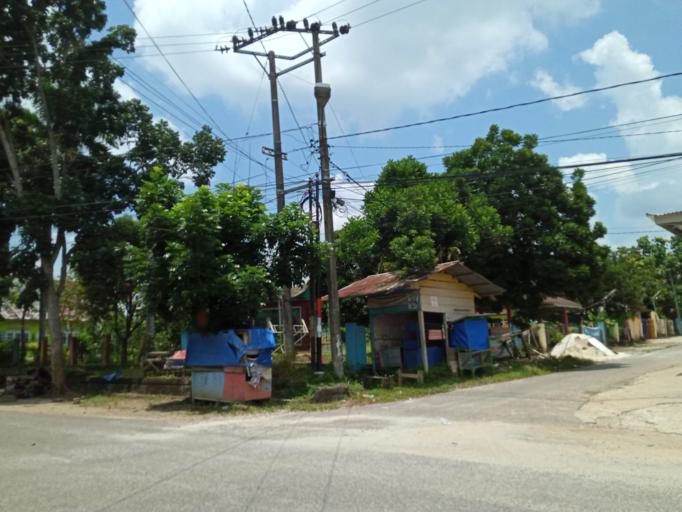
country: ID
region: Jambi
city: Bangko
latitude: -2.0596
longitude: 102.2766
